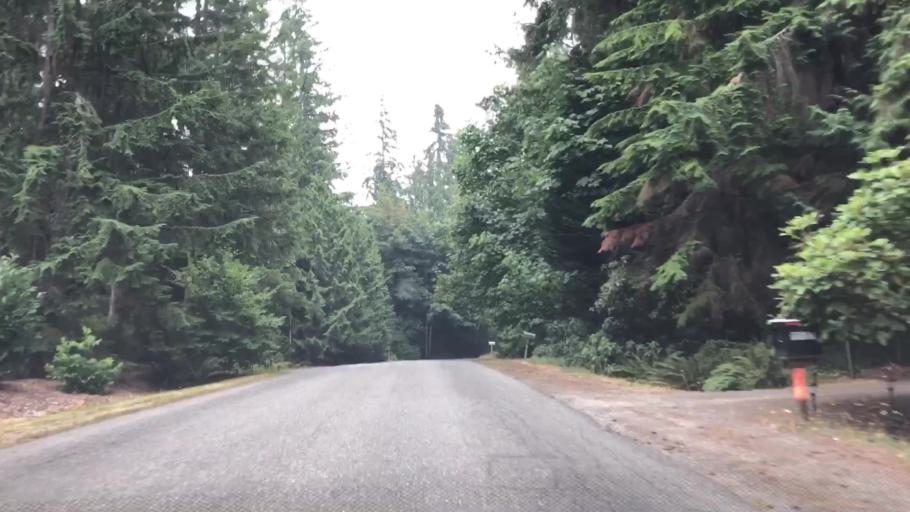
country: US
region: Washington
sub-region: King County
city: Cottage Lake
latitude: 47.7693
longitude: -122.0773
